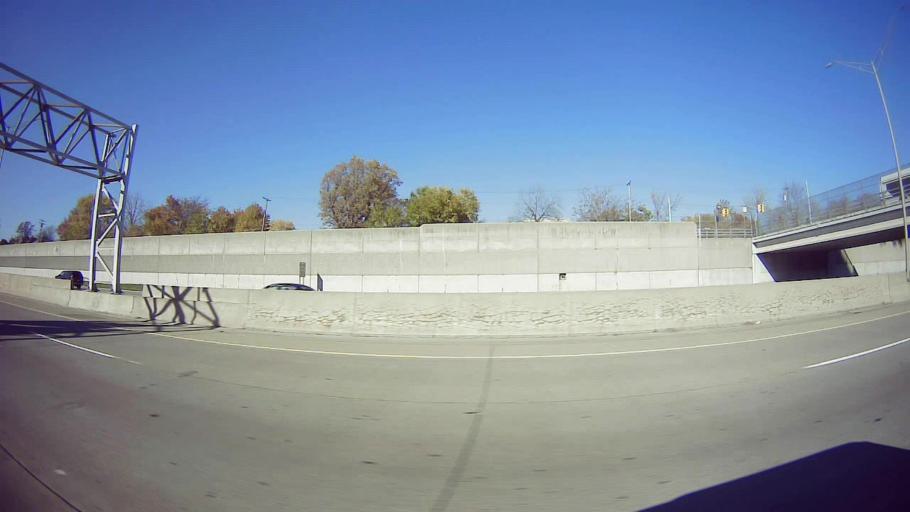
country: US
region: Michigan
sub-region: Wayne County
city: Highland Park
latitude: 42.4008
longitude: -83.1019
